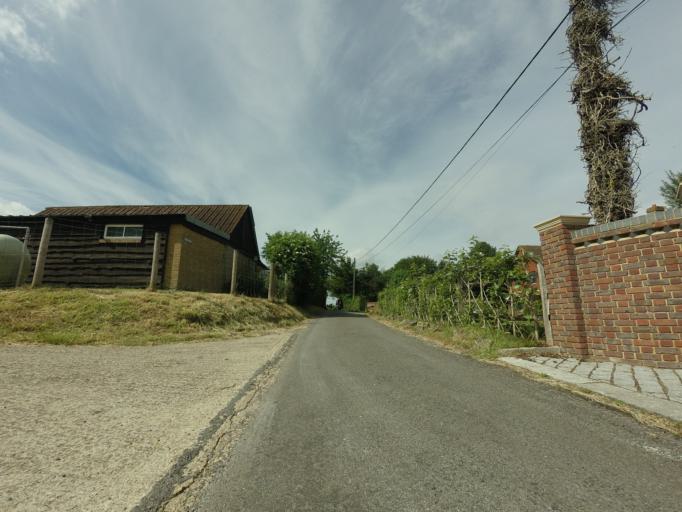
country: GB
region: England
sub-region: Greater London
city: Orpington
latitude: 51.3711
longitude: 0.1342
